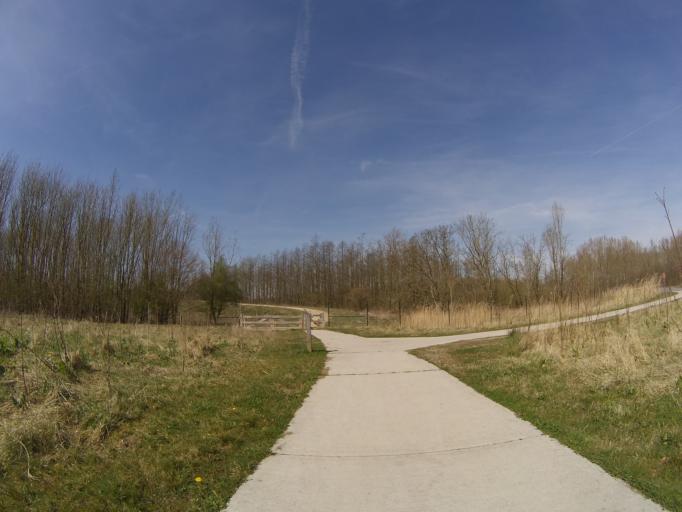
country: NL
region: Flevoland
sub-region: Gemeente Zeewolde
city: Zeewolde
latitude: 52.3144
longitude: 5.4694
